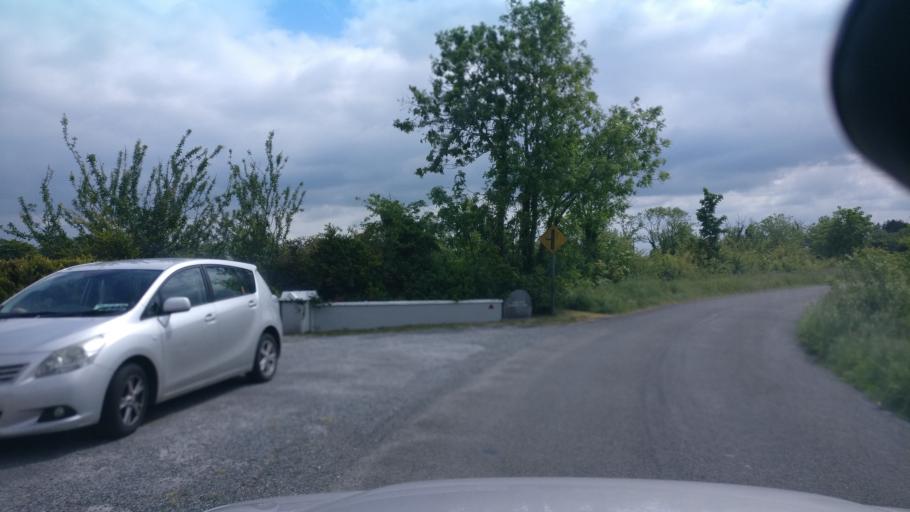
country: IE
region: Connaught
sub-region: County Galway
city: Ballinasloe
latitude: 53.2784
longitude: -8.3391
